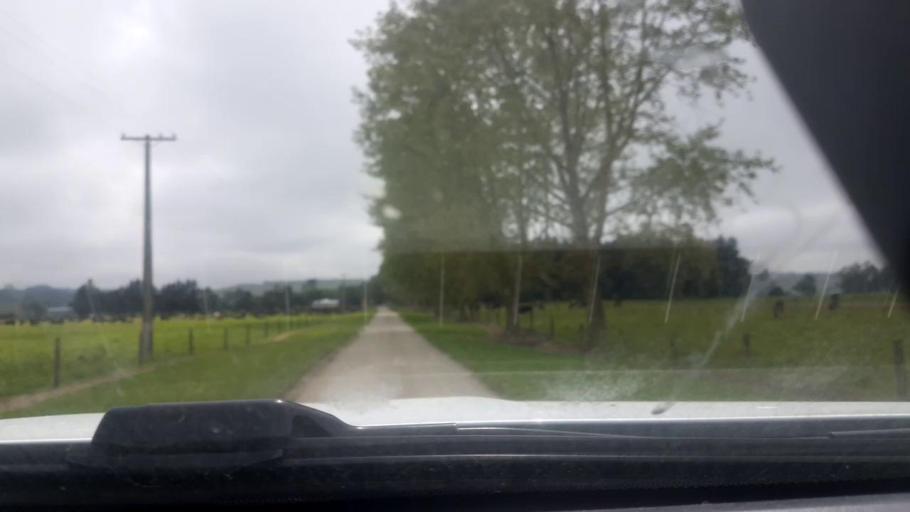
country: NZ
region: Canterbury
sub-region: Timaru District
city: Pleasant Point
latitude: -44.2103
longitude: 171.1108
